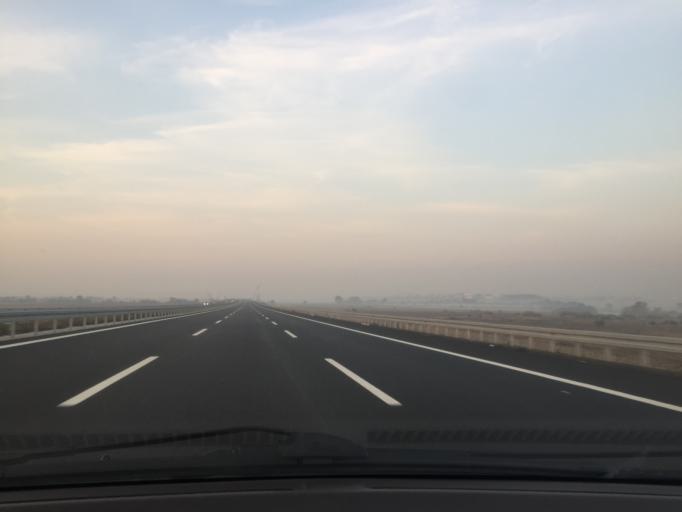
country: TR
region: Bursa
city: Karacabey
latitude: 40.2300
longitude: 28.4132
